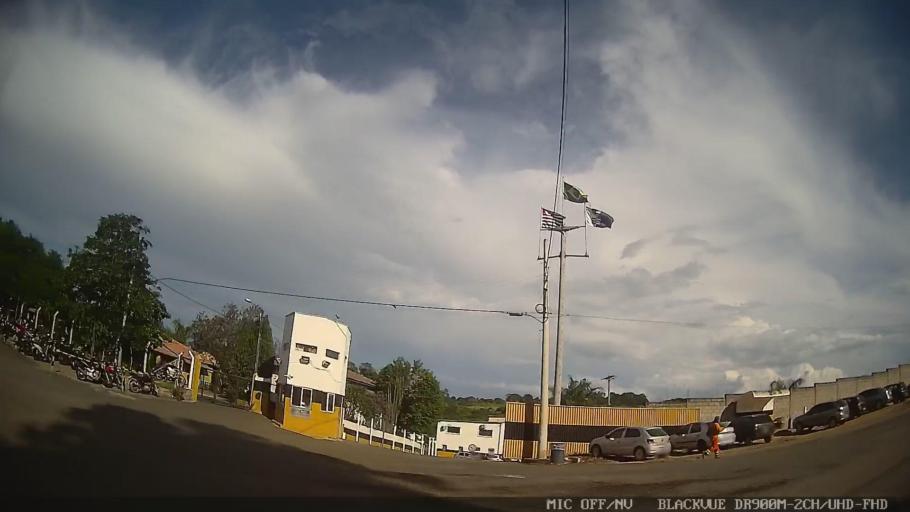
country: BR
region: Sao Paulo
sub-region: Tiete
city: Tiete
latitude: -23.1139
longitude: -47.6977
